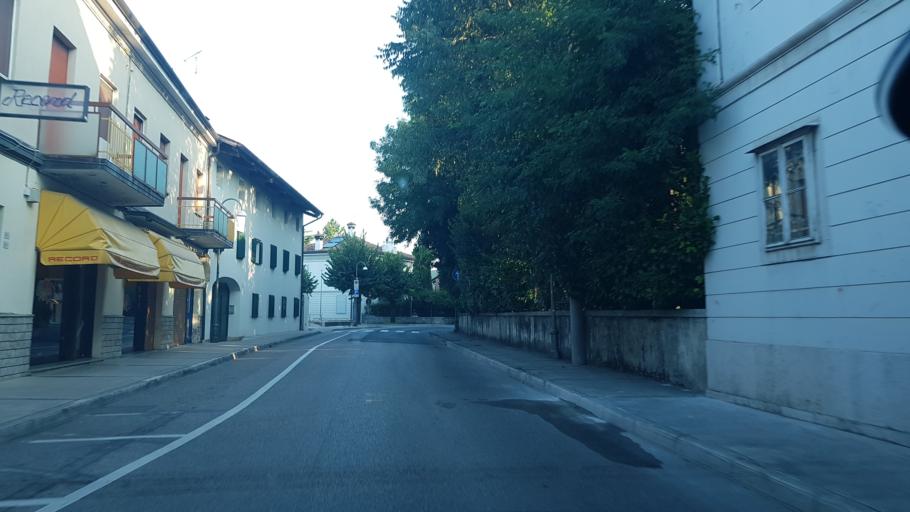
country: IT
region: Friuli Venezia Giulia
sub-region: Provincia di Gorizia
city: Ronchi dei Legionari
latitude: 45.8247
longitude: 13.5001
